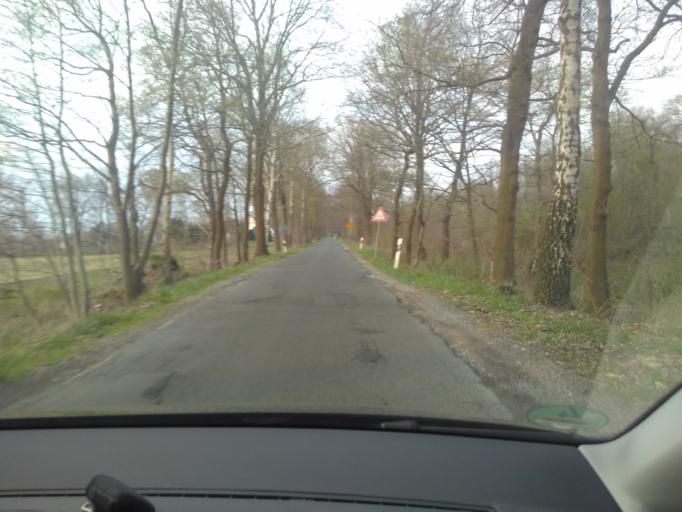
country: DE
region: Lower Saxony
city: Adelheidsdorf
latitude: 52.5396
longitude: 10.0348
